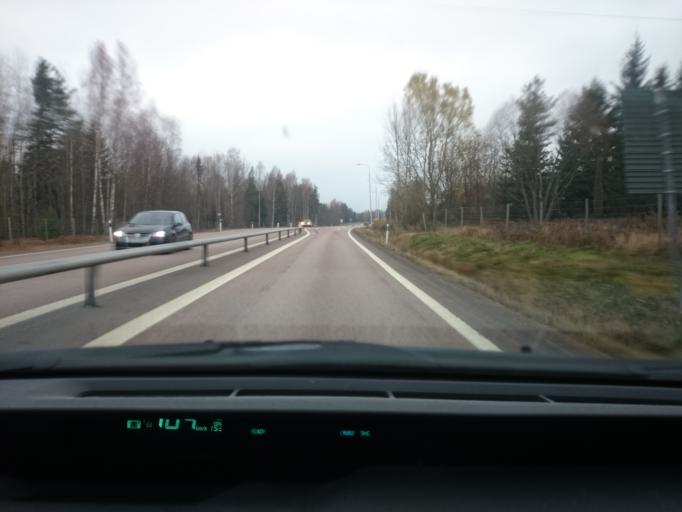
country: SE
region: Dalarna
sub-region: Avesta Kommun
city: Avesta
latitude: 60.1678
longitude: 16.1504
